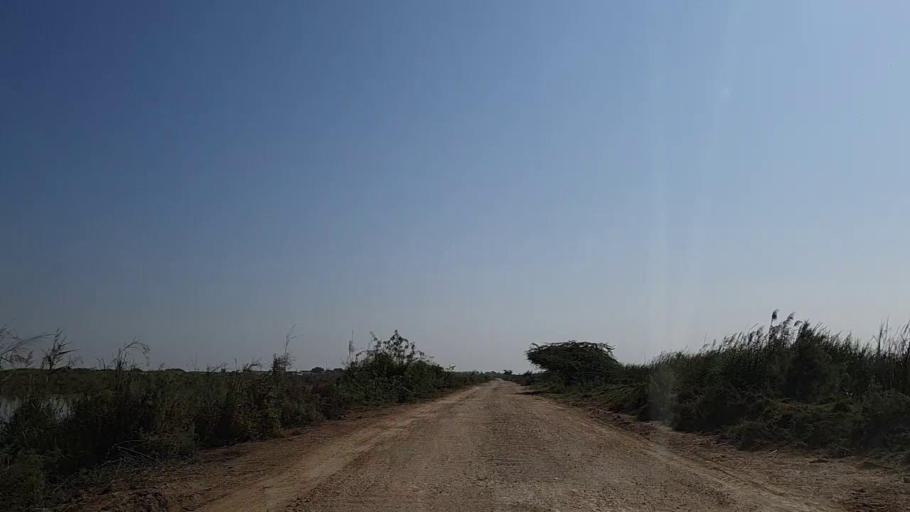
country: PK
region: Sindh
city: Chuhar Jamali
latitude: 24.4656
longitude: 68.0997
